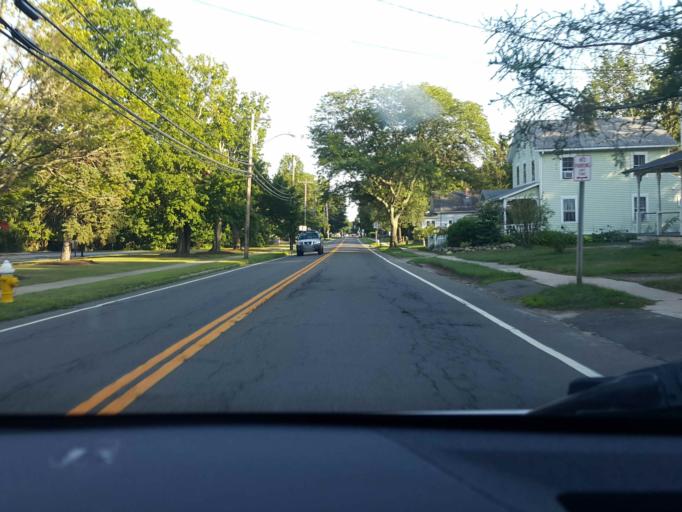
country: US
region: Connecticut
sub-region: New Haven County
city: Guilford
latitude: 41.2921
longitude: -72.6858
